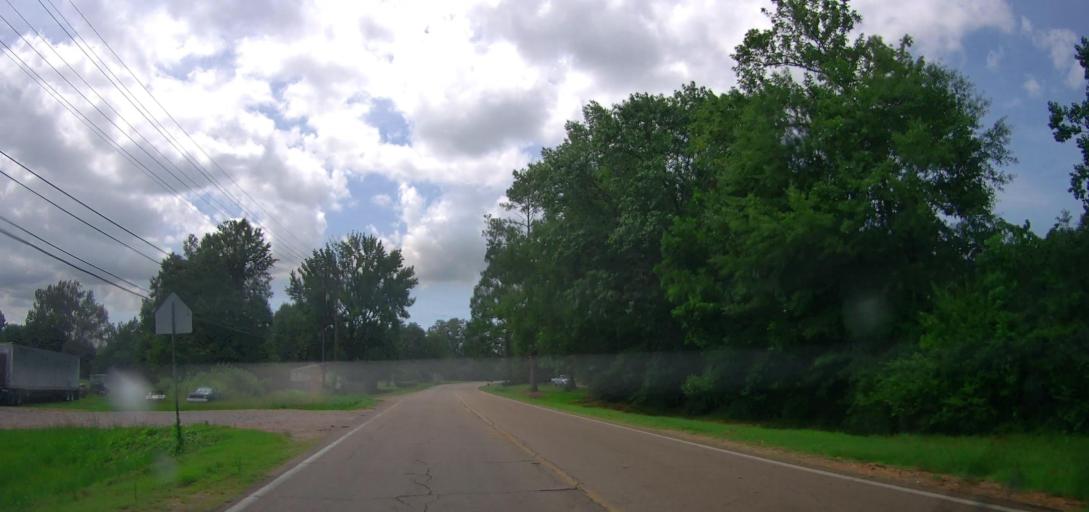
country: US
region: Mississippi
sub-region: Lee County
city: Shannon
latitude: 34.1225
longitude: -88.7150
